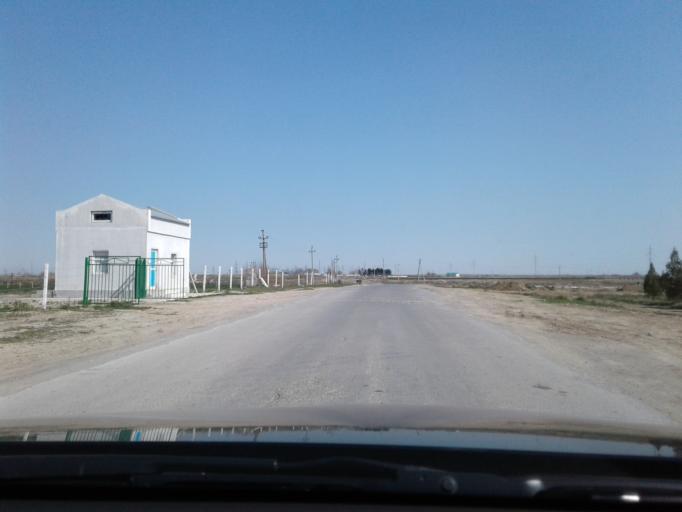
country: TM
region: Ahal
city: Abadan
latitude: 38.0964
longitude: 58.2007
